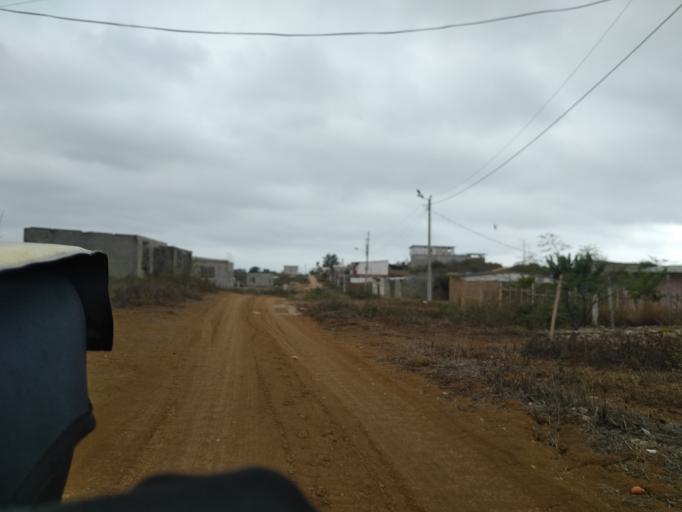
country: EC
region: Santa Elena
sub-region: Canton Santa Elena
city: Santa Elena
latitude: -2.2054
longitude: -80.8640
